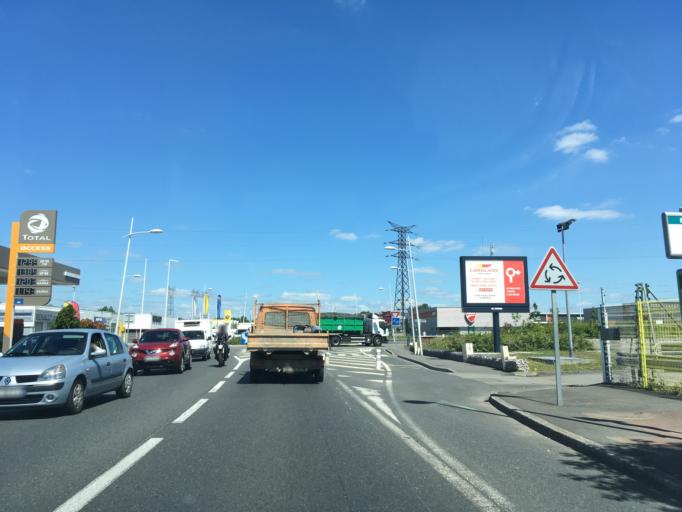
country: FR
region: Pays de la Loire
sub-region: Departement de la Loire-Atlantique
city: Les Sorinieres
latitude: 47.1548
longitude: -1.5369
